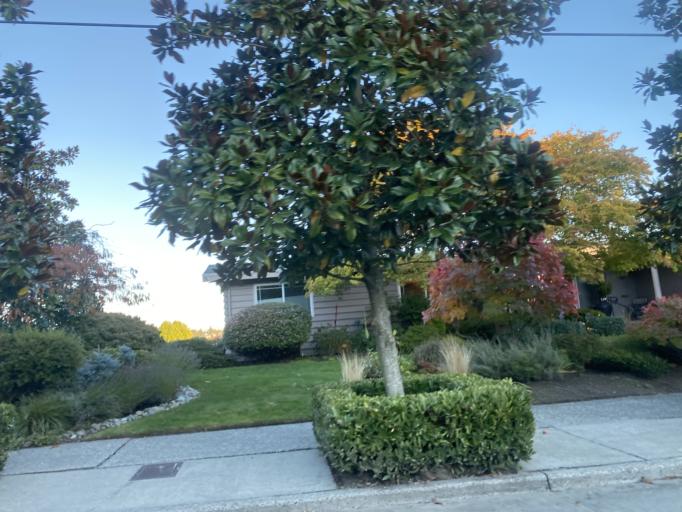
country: US
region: Washington
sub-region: King County
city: Seattle
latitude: 47.6411
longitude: -122.3904
